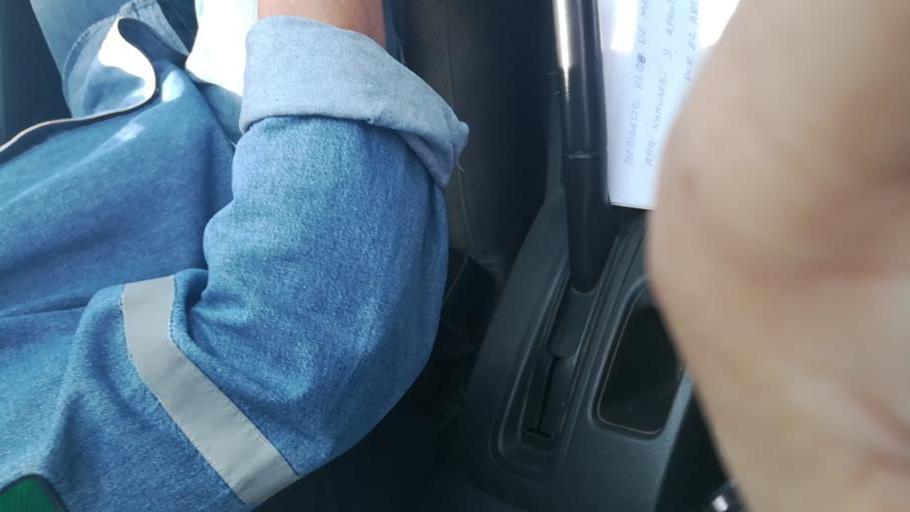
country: EC
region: Napo
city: Tena
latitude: -0.9883
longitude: -77.8203
